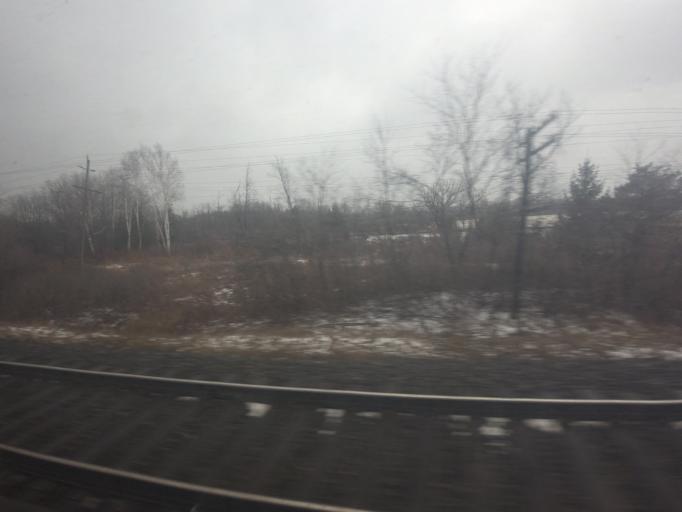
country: CA
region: Ontario
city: Quinte West
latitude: 44.0307
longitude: -77.7600
